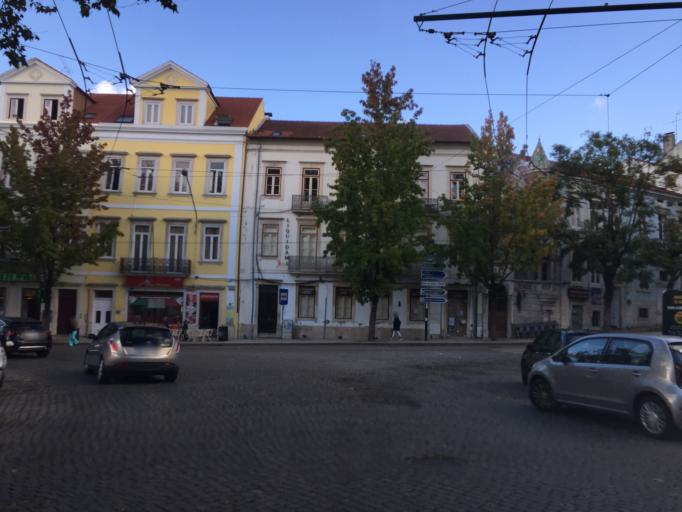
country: PT
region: Coimbra
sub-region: Coimbra
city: Coimbra
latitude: 40.2096
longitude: -8.4192
